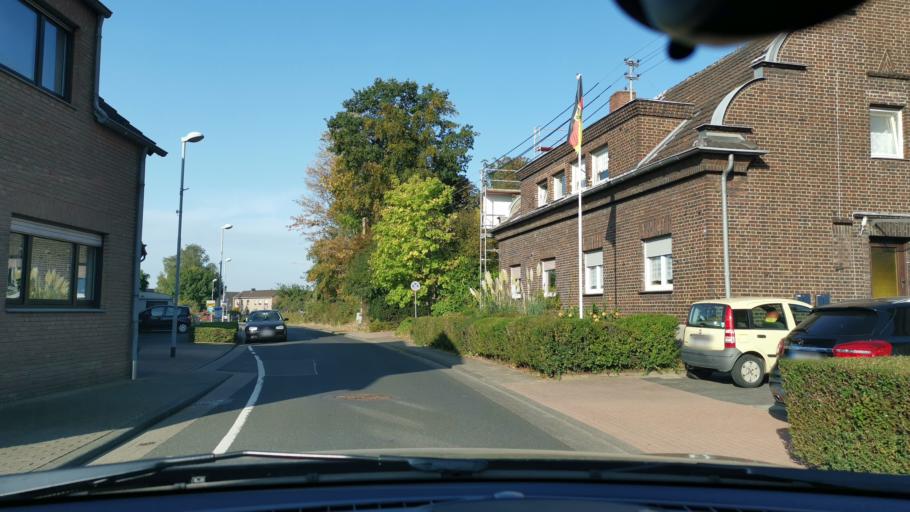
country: DE
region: North Rhine-Westphalia
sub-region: Regierungsbezirk Dusseldorf
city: Neubrueck
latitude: 51.0991
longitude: 6.6756
